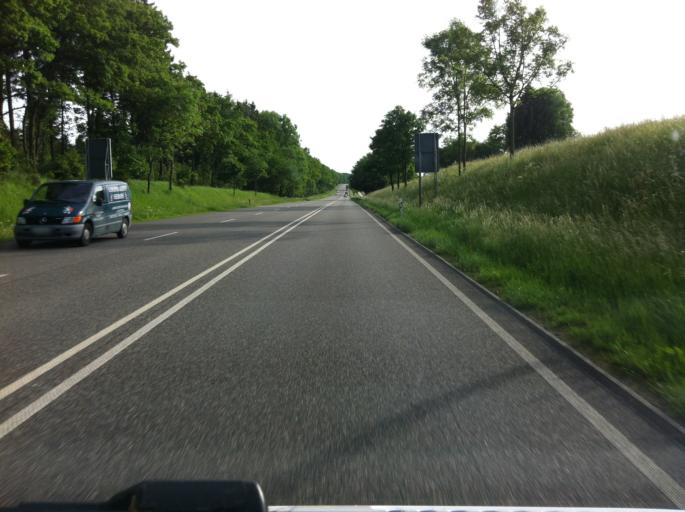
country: DE
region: North Rhine-Westphalia
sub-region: Regierungsbezirk Koln
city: Blankenheim
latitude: 50.4253
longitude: 6.6007
